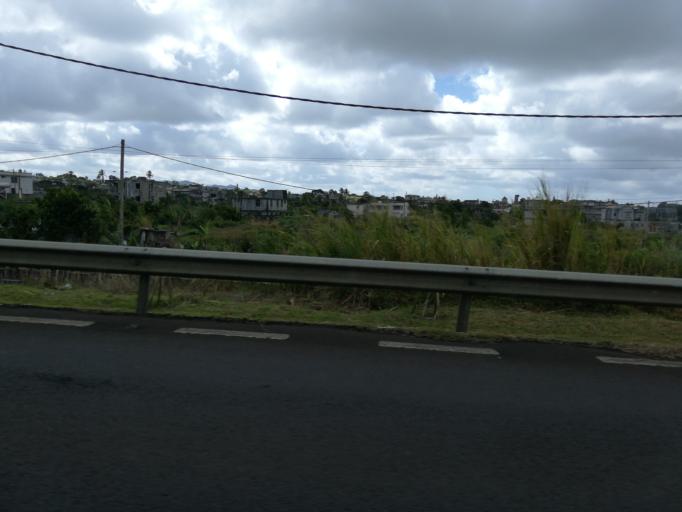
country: MU
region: Grand Port
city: Rose Belle
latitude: -20.3950
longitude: 57.5795
